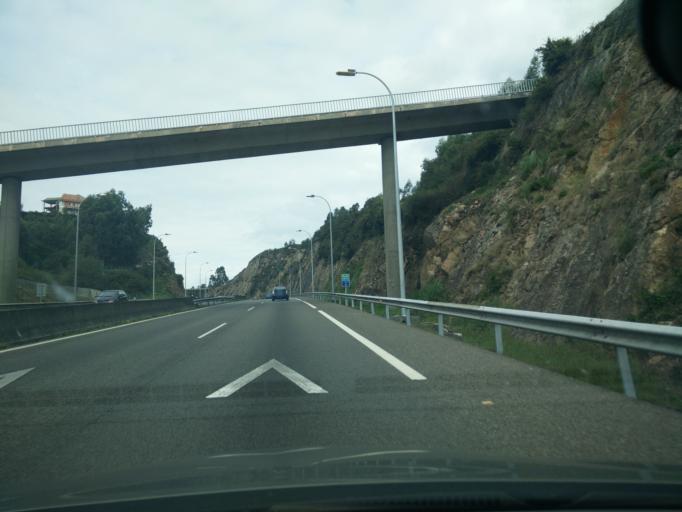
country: ES
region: Galicia
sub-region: Provincia da Coruna
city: Culleredo
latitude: 43.3207
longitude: -8.3924
